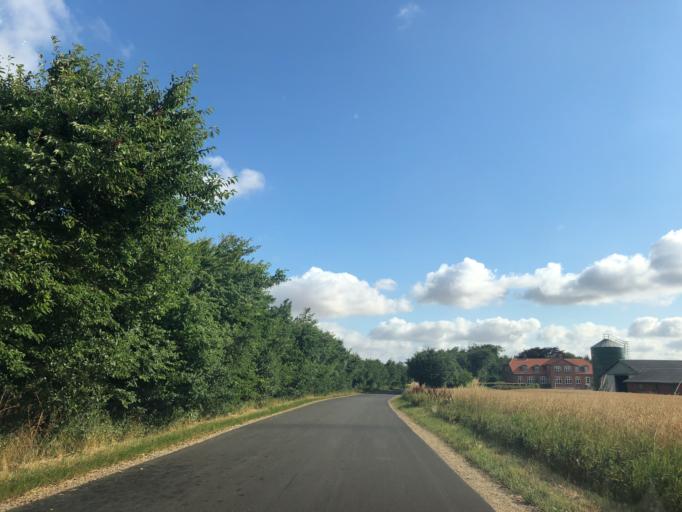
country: DK
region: Central Jutland
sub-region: Holstebro Kommune
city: Vinderup
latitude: 56.6187
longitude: 8.8716
